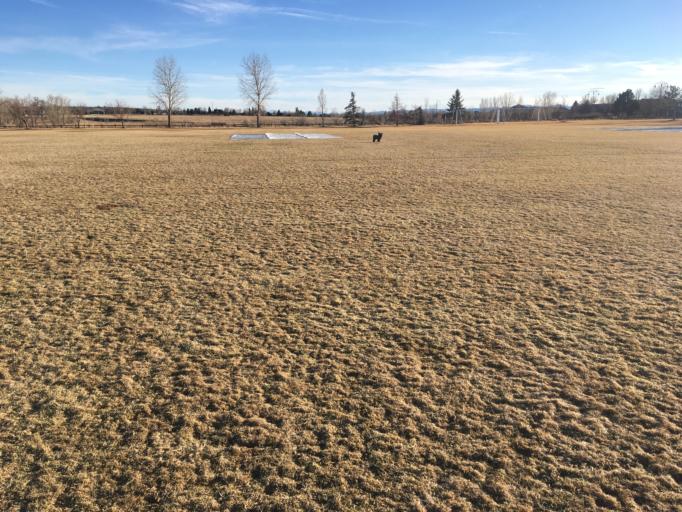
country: US
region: Colorado
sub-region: Broomfield County
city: Broomfield
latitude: 39.9350
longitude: -105.0517
